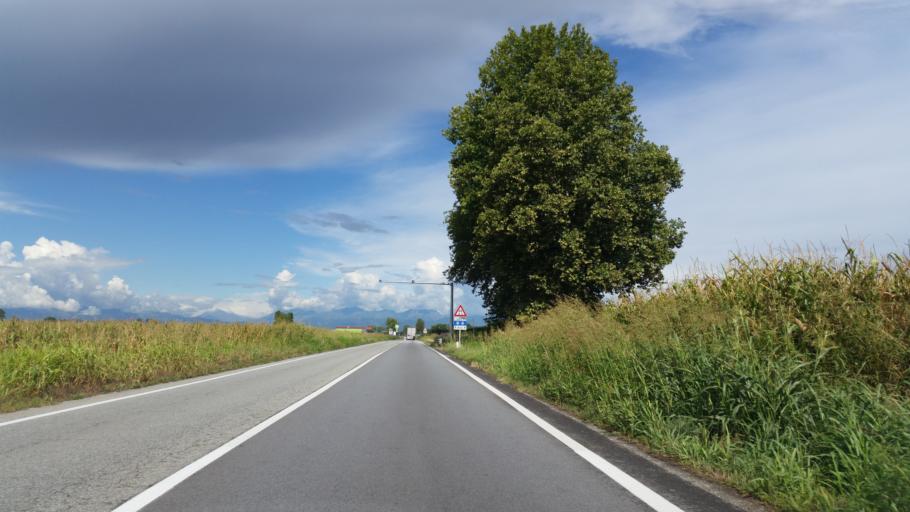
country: IT
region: Piedmont
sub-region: Provincia di Torino
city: Marocchi
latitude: 44.9447
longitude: 7.8116
